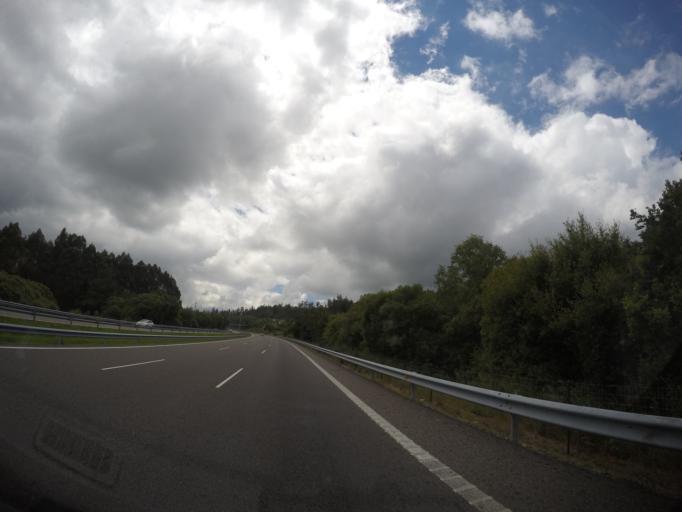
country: ES
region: Galicia
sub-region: Provincia da Coruna
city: Abegondo
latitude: 43.1936
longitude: -8.3082
